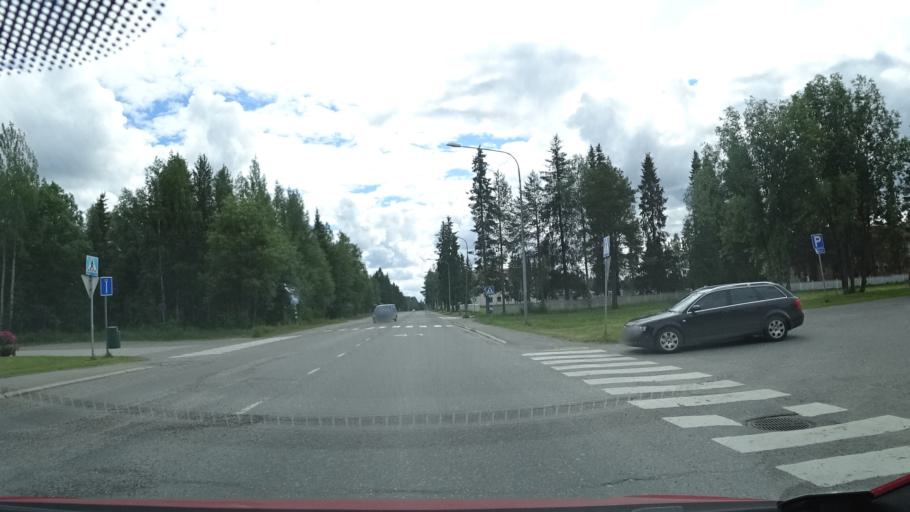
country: FI
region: Lapland
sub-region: Tunturi-Lappi
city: Kittilae
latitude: 67.6530
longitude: 24.9131
